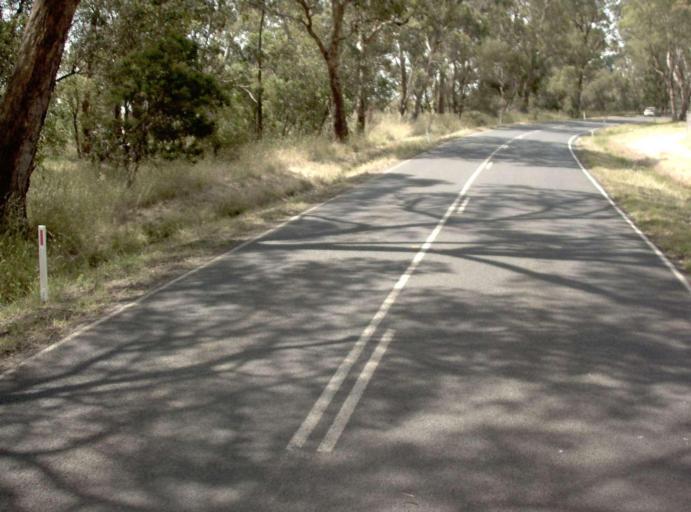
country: AU
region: Victoria
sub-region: Latrobe
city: Traralgon
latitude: -38.2607
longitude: 146.5468
